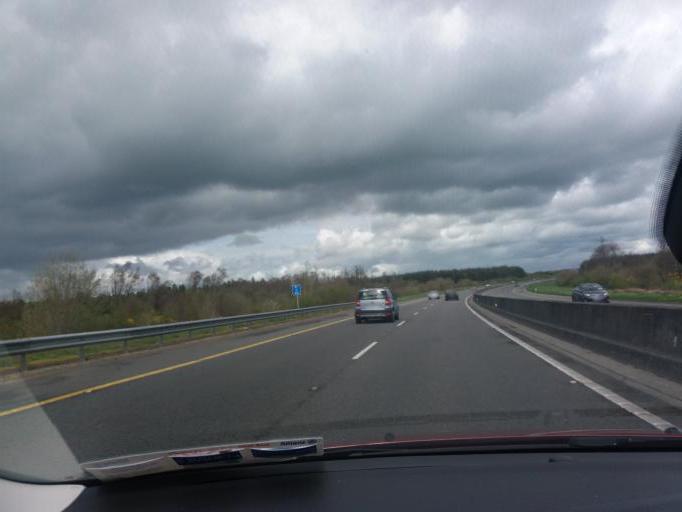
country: IE
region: Leinster
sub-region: Laois
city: Mountrath
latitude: 52.9839
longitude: -7.4327
